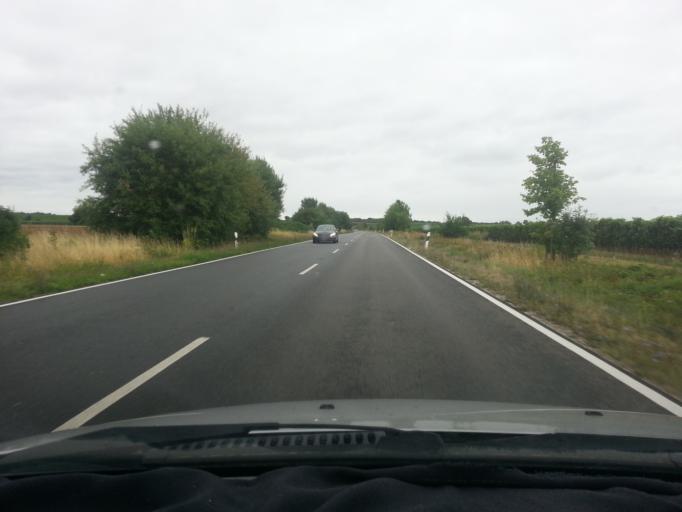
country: DE
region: Rheinland-Pfalz
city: Ruppertsberg
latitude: 49.3933
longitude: 8.2130
